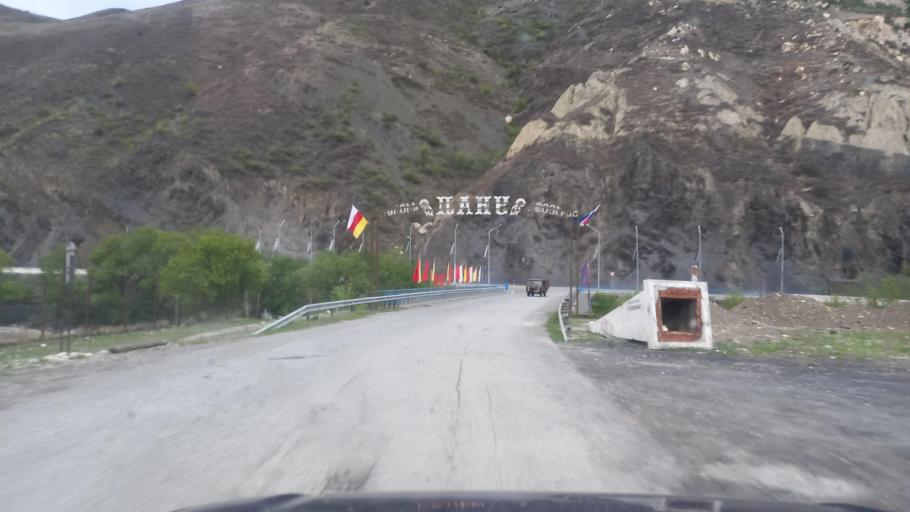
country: RU
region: North Ossetia
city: Mizur
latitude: 42.8613
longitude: 44.1448
